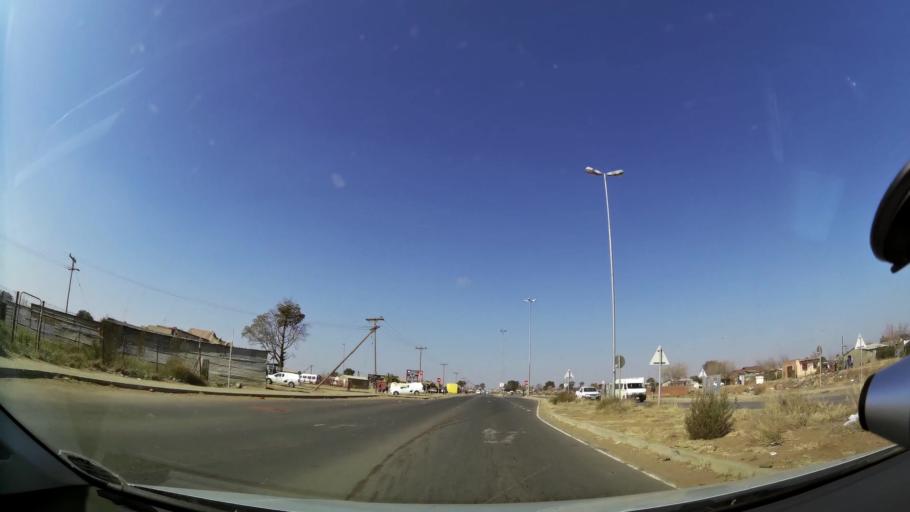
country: ZA
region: Orange Free State
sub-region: Mangaung Metropolitan Municipality
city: Bloemfontein
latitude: -29.1577
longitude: 26.2758
